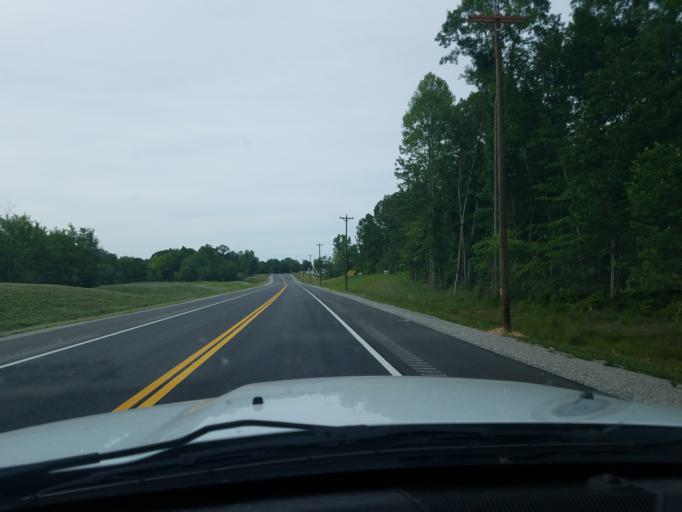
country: US
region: Tennessee
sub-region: Putnam County
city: Cookeville
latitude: 36.1718
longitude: -85.5617
